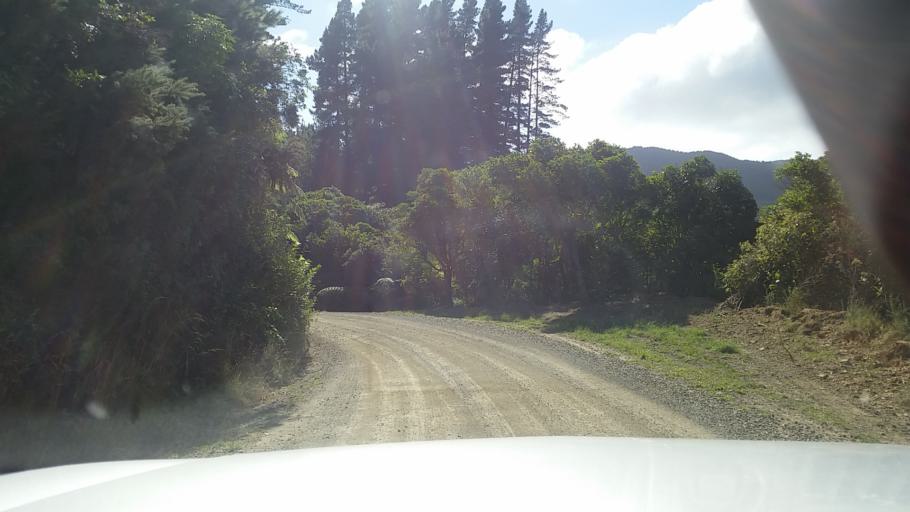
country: NZ
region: Marlborough
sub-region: Marlborough District
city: Picton
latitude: -41.2883
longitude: 174.1732
